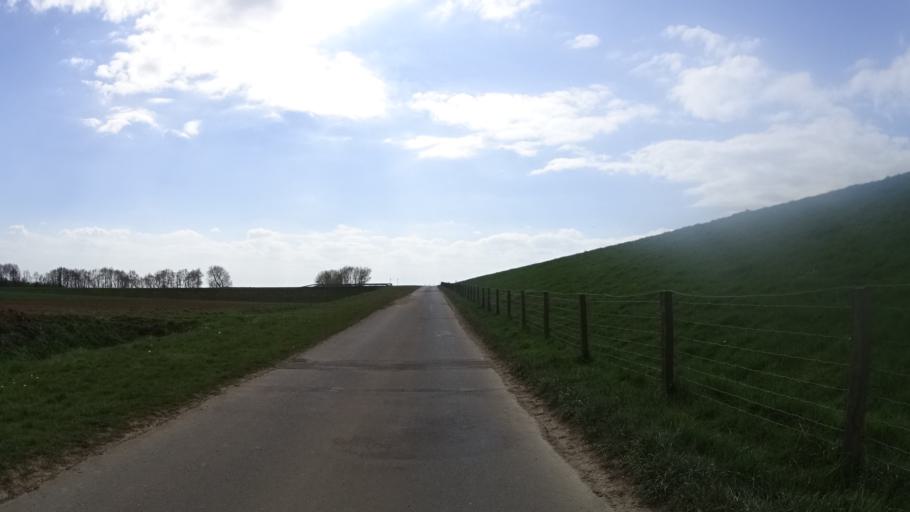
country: DE
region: Lower Saxony
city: Rhede
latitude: 53.0955
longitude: 7.2993
